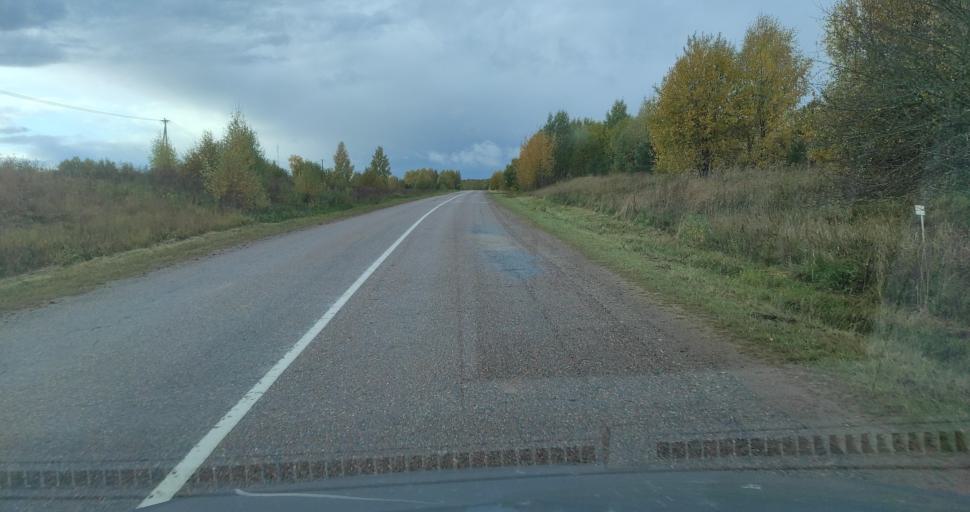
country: LV
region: Skrunda
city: Skrunda
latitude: 56.5877
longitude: 21.8984
